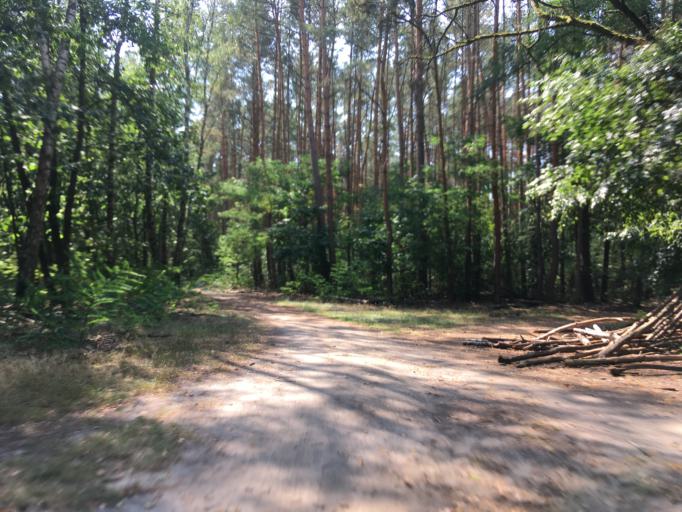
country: DE
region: Berlin
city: Friedrichshagen
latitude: 52.4717
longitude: 13.6071
